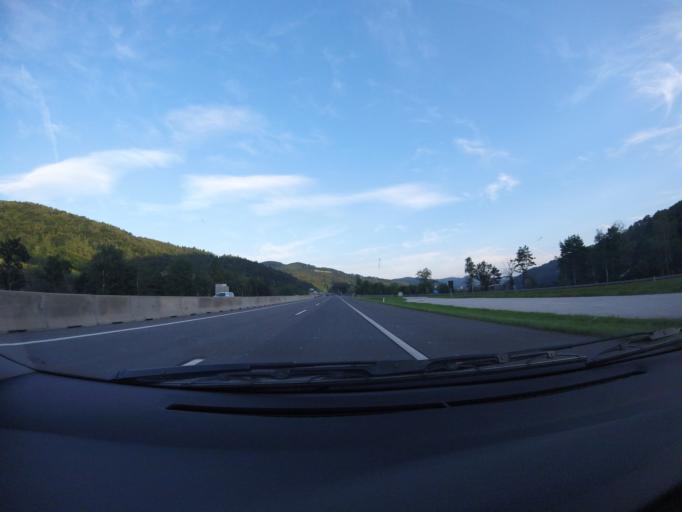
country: AT
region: Lower Austria
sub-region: Politischer Bezirk Neunkirchen
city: Grimmenstein
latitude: 47.6310
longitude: 16.1295
